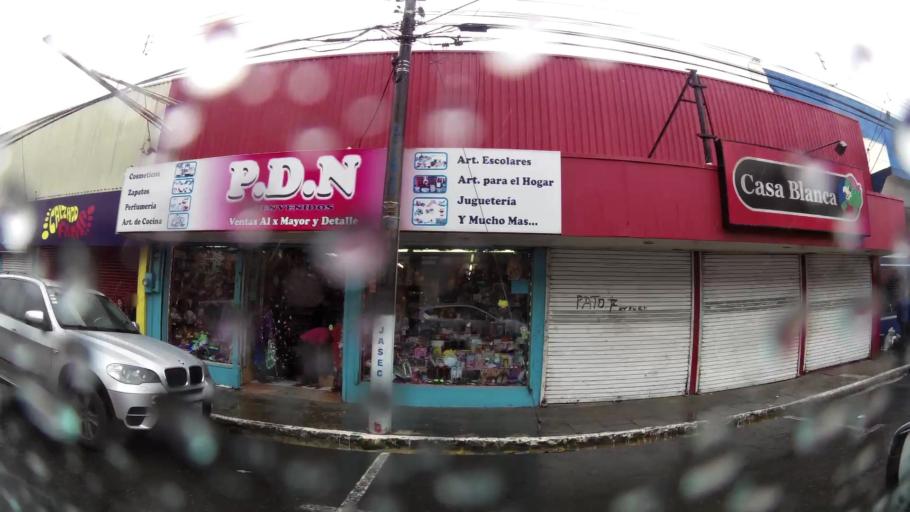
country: CR
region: Cartago
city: Cartago
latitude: 9.8652
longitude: -83.9187
